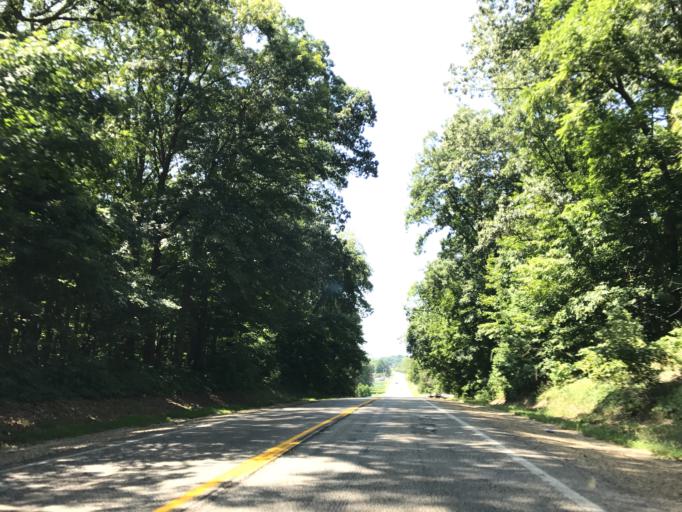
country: US
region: Michigan
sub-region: Berrien County
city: Buchanan
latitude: 41.8052
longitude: -86.3826
